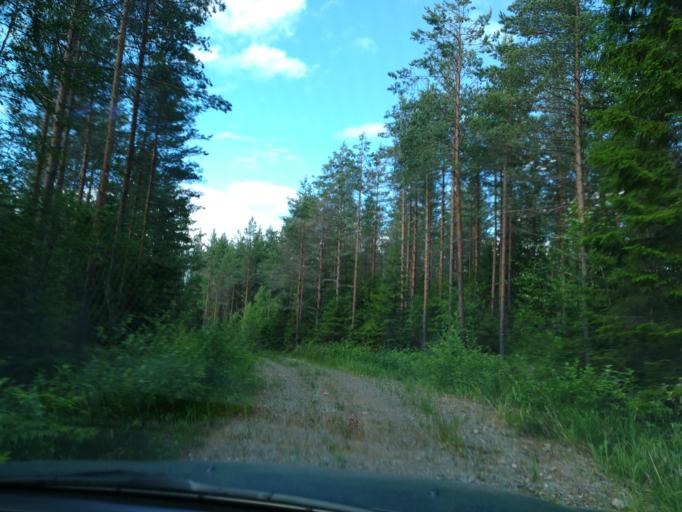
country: FI
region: South Karelia
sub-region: Lappeenranta
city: Savitaipale
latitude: 61.3018
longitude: 27.6186
